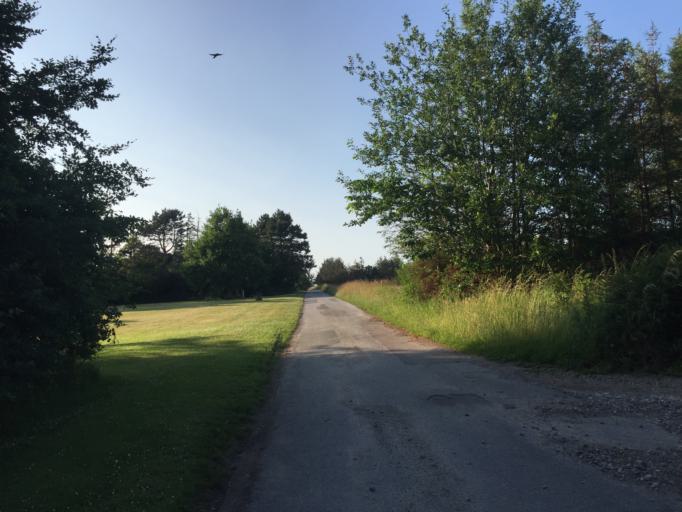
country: DK
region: Zealand
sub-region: Slagelse Kommune
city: Korsor
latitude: 55.2321
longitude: 11.1749
